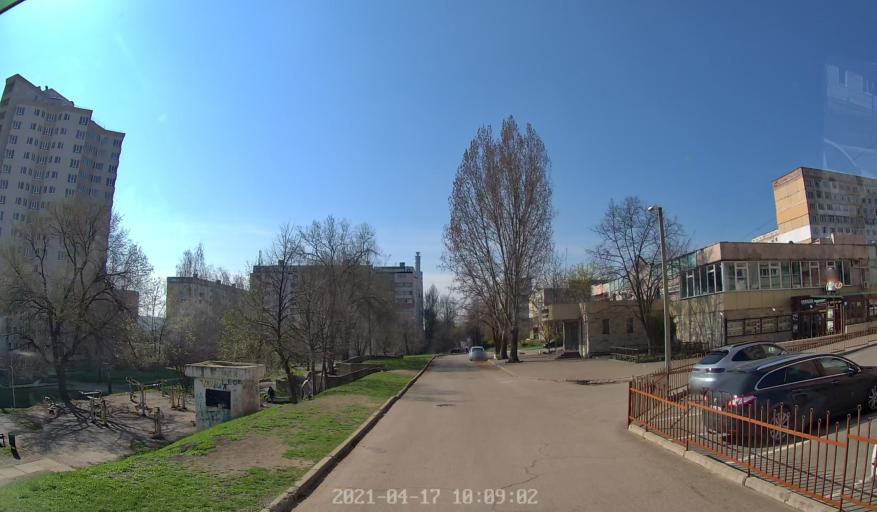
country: MD
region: Chisinau
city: Chisinau
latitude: 47.0406
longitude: 28.8928
